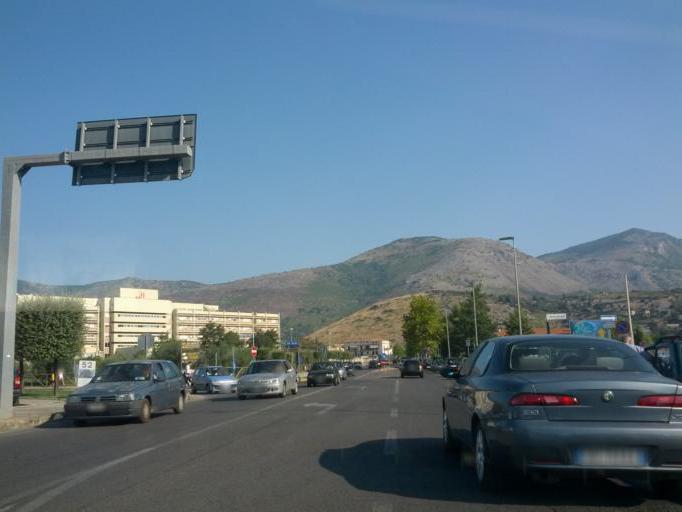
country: IT
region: Latium
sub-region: Provincia di Latina
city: Fondi
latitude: 41.3592
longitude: 13.4172
